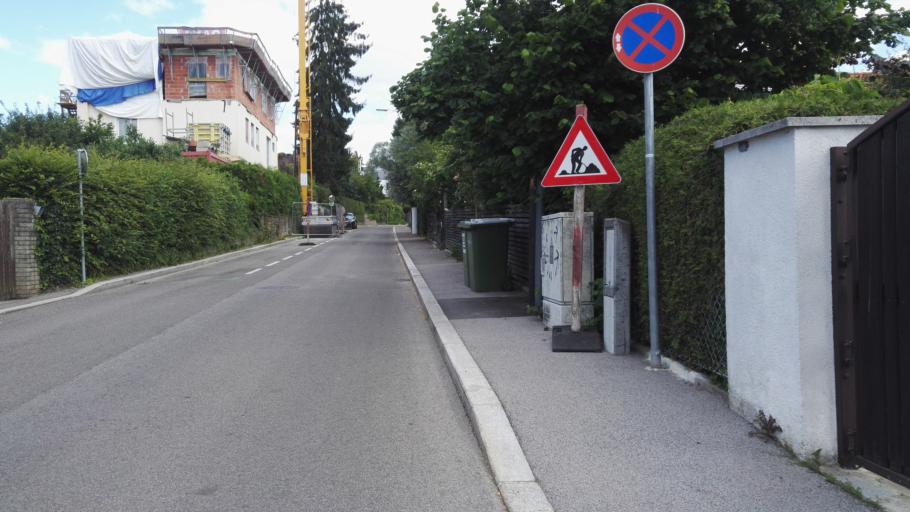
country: AT
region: Styria
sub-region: Graz Stadt
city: Graz
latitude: 47.0711
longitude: 15.4687
